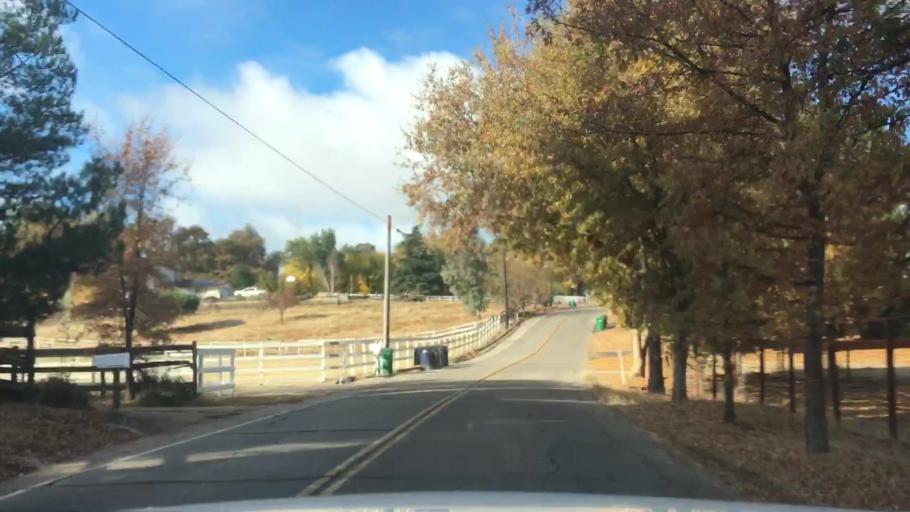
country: US
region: California
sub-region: San Luis Obispo County
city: Atascadero
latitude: 35.4581
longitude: -120.6611
